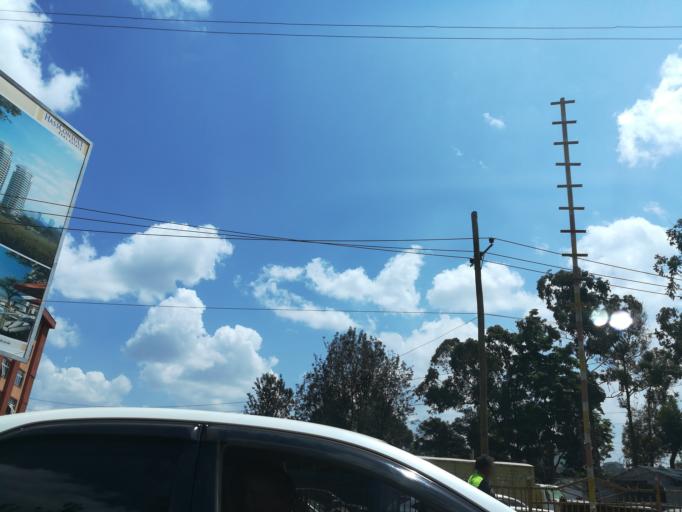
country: KE
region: Nairobi Area
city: Nairobi
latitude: -1.3119
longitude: 36.8164
